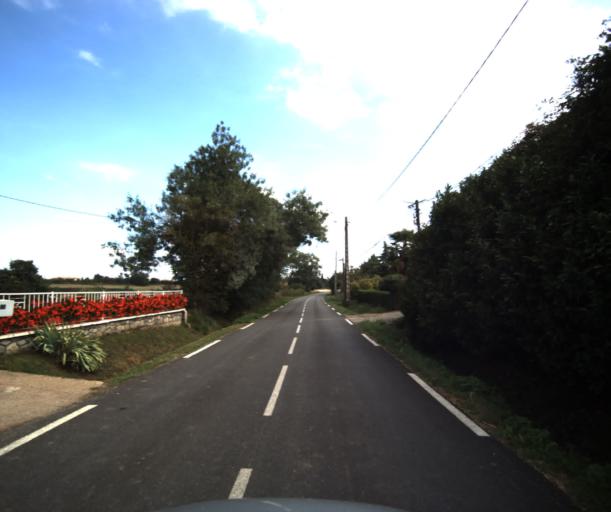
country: FR
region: Midi-Pyrenees
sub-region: Departement de la Haute-Garonne
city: Lacasse
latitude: 43.3990
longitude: 1.2565
